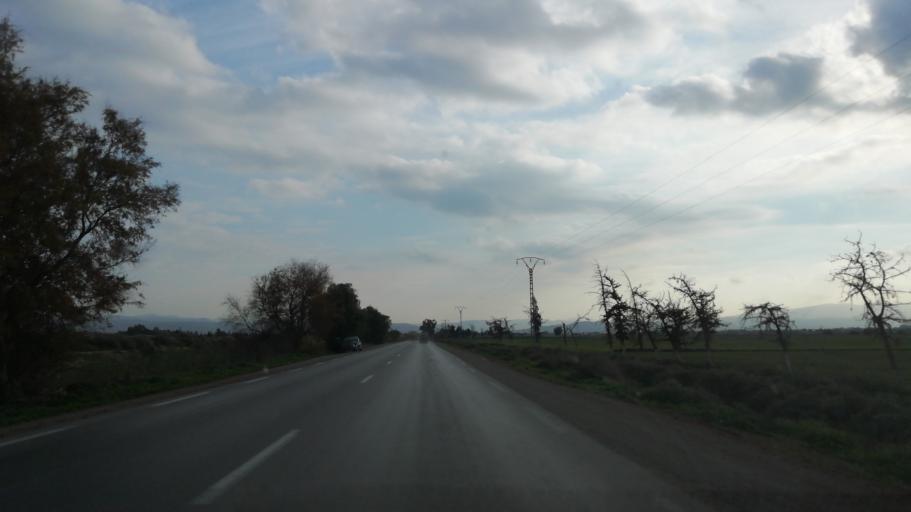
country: DZ
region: Mascara
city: Mascara
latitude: 35.6509
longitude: 0.0595
